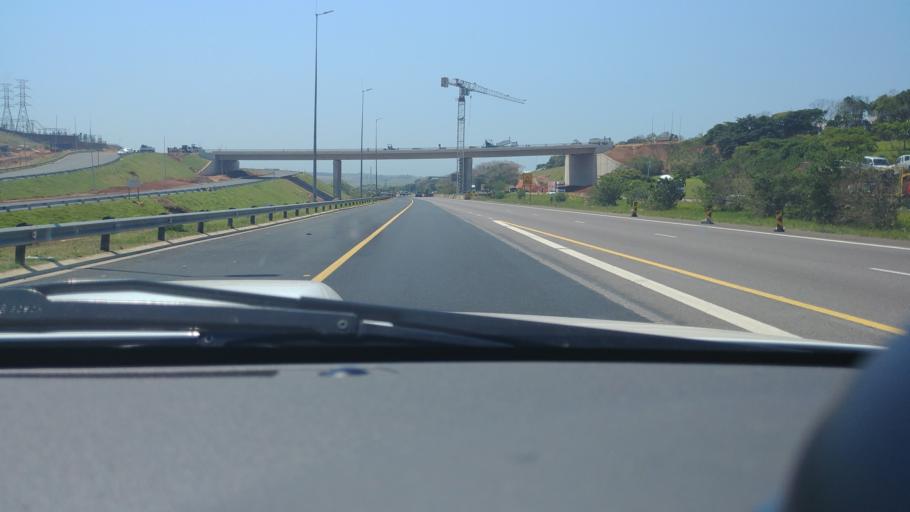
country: ZA
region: KwaZulu-Natal
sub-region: eThekwini Metropolitan Municipality
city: Durban
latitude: -29.7173
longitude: 31.0617
